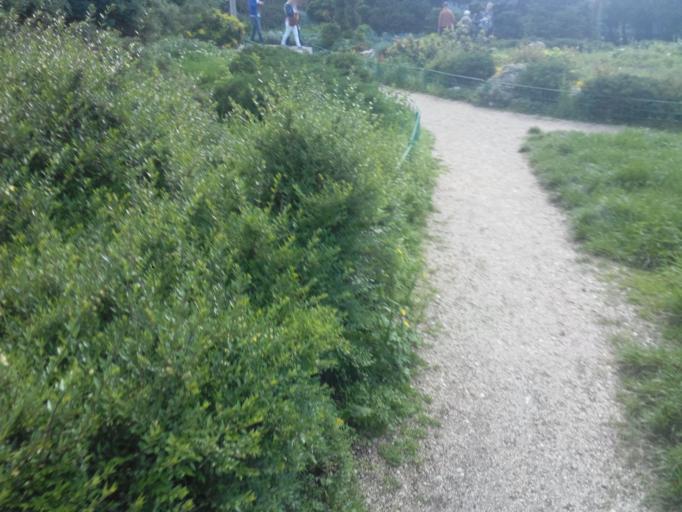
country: RO
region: Bucuresti
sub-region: Municipiul Bucuresti
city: Bucuresti
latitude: 44.4372
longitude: 26.0664
